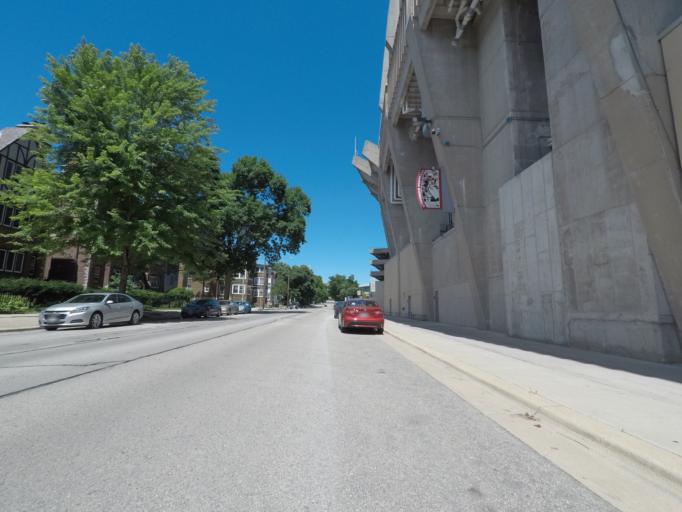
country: US
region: Wisconsin
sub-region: Dane County
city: Madison
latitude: 43.0698
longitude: -89.4139
